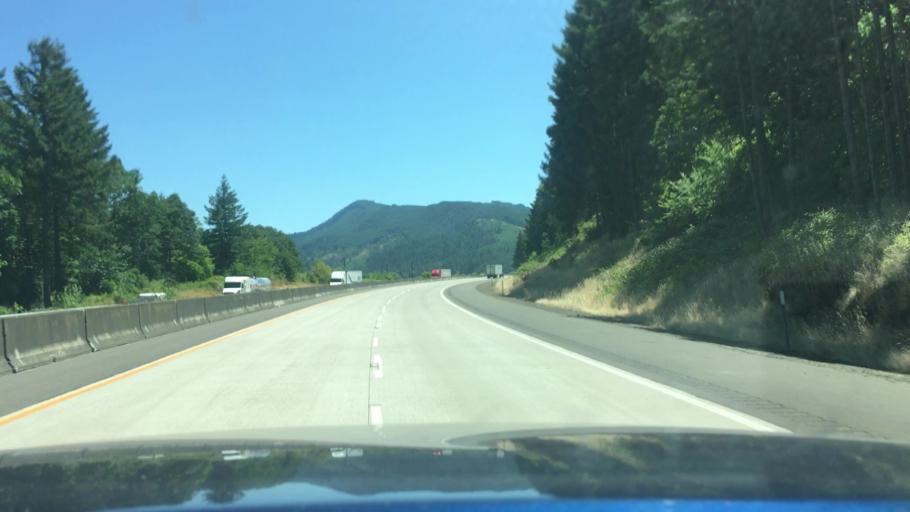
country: US
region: Oregon
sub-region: Douglas County
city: Yoncalla
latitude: 43.6202
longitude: -123.2150
